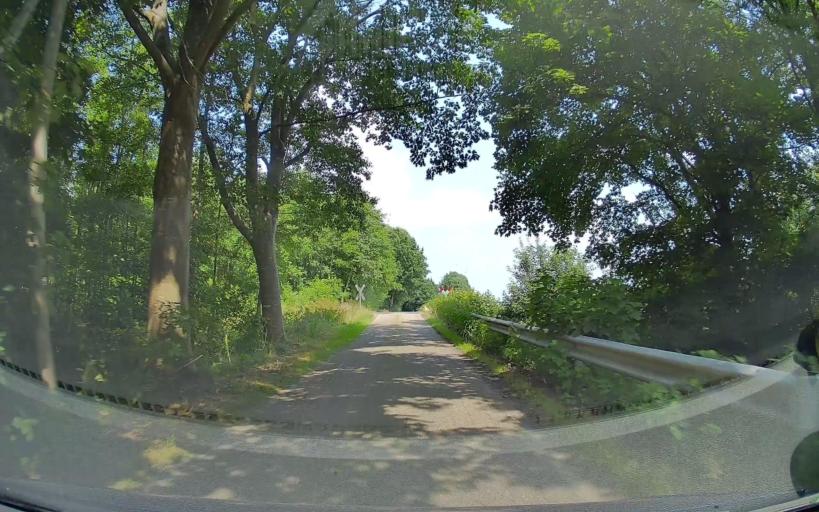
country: DE
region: Lower Saxony
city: Bosel
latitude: 53.0110
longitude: 7.9095
